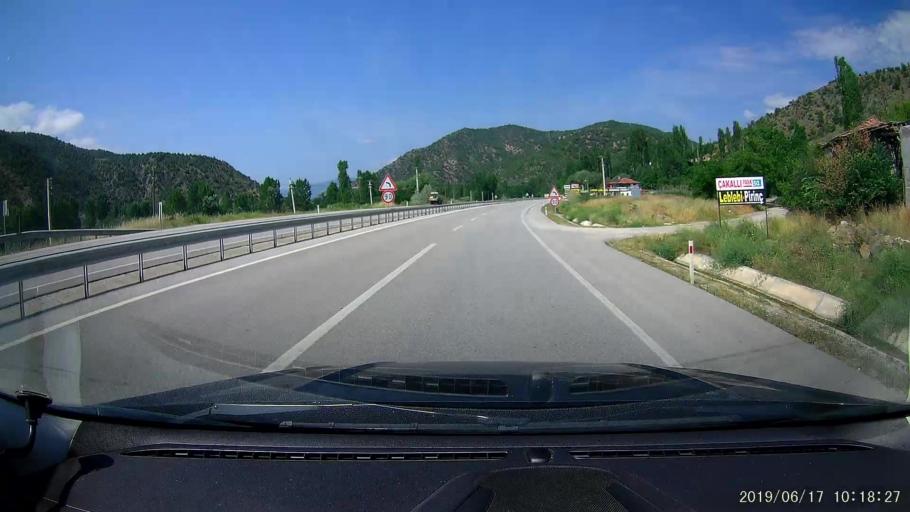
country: TR
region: Corum
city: Osmancik
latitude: 40.9784
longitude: 34.9221
